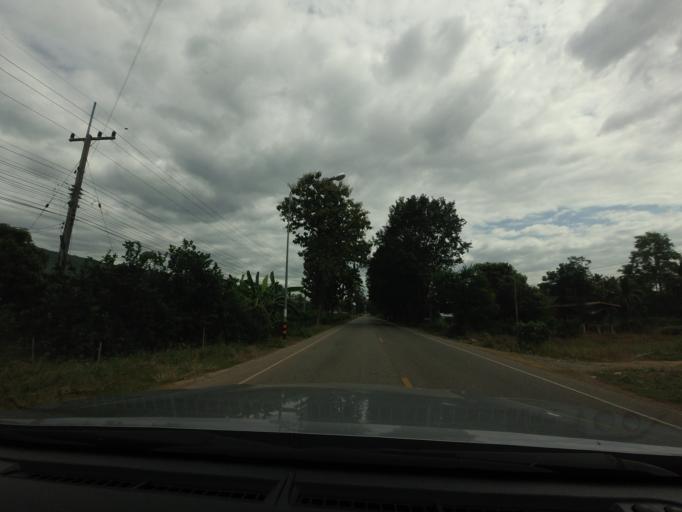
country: TH
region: Phitsanulok
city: Wang Thong
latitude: 16.7053
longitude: 100.5073
